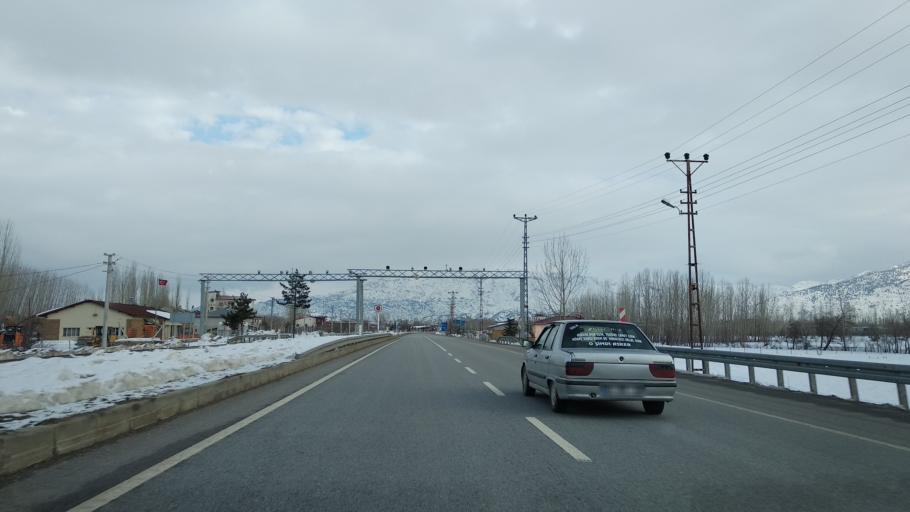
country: TR
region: Kahramanmaras
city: Goksun
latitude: 38.0318
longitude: 36.4733
